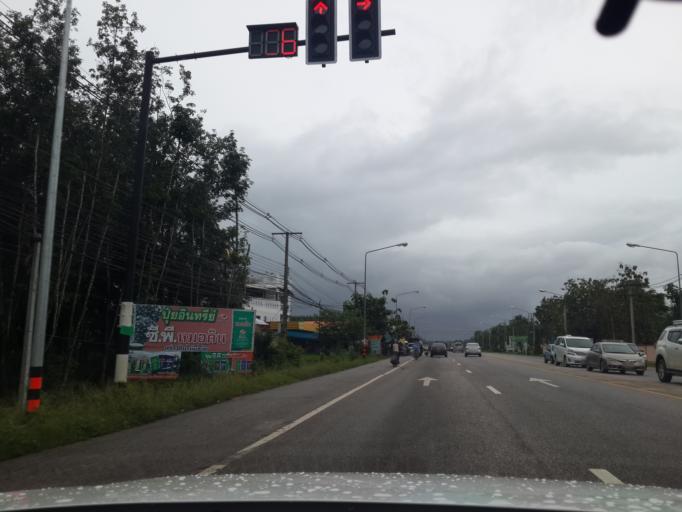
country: TH
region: Songkhla
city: Khlong Hoi Khong
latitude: 6.9588
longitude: 100.4227
